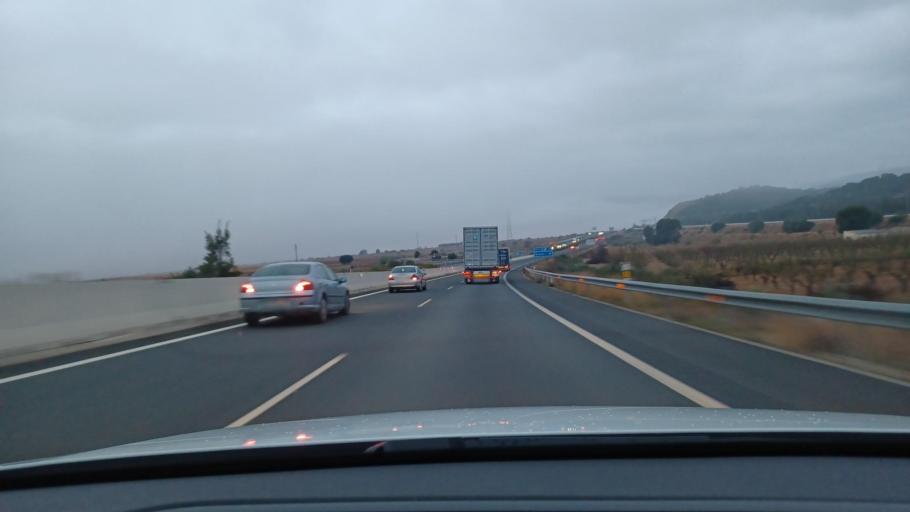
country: ES
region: Valencia
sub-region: Provincia de Valencia
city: La Font de la Figuera
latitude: 38.8394
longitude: -0.8567
